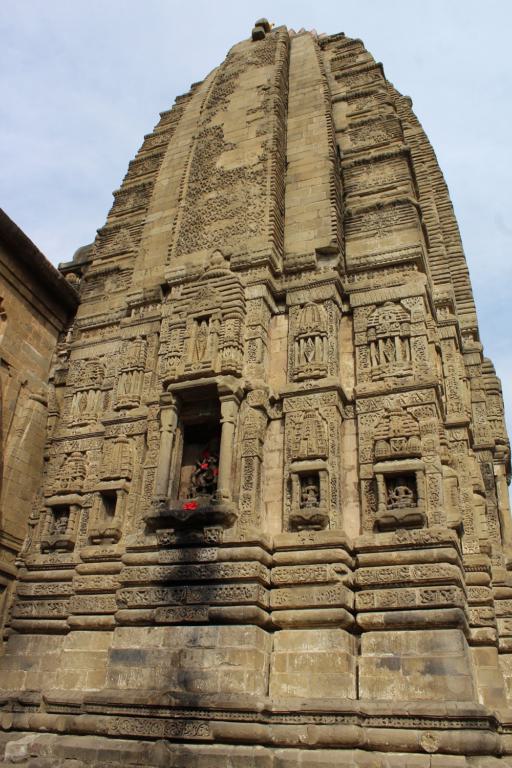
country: IN
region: Himachal Pradesh
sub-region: Kangra
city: Palampur
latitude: 32.0508
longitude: 76.6459
